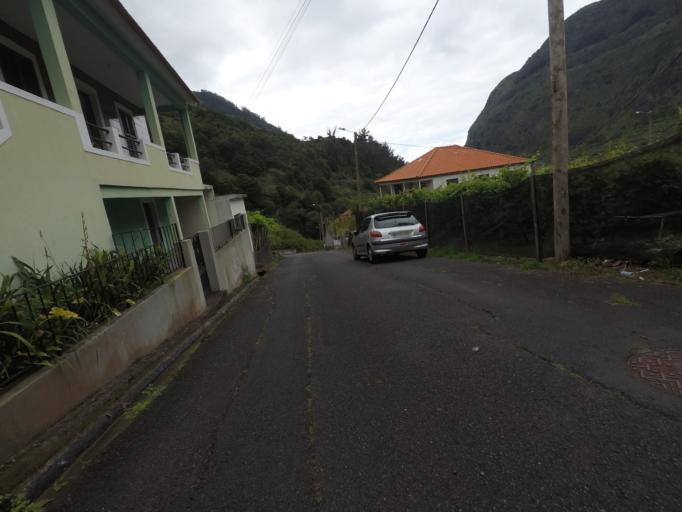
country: PT
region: Madeira
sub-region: Sao Vicente
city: Sao Vicente
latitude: 32.7949
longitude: -17.0427
